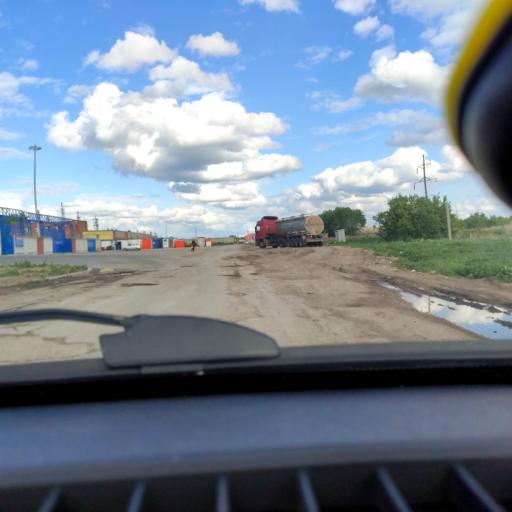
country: RU
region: Samara
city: Tol'yatti
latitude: 53.5471
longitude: 49.4709
